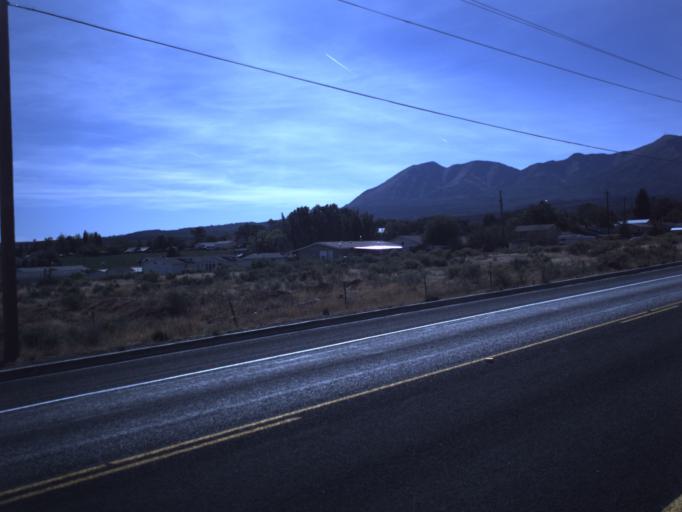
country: US
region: Utah
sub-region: San Juan County
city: Monticello
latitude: 37.8728
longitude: -109.3327
